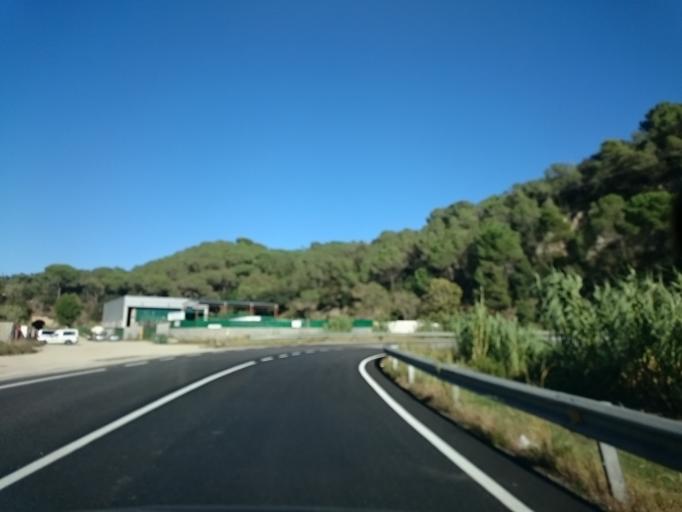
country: ES
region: Catalonia
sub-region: Provincia de Barcelona
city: Capellades
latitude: 41.5237
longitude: 1.7063
